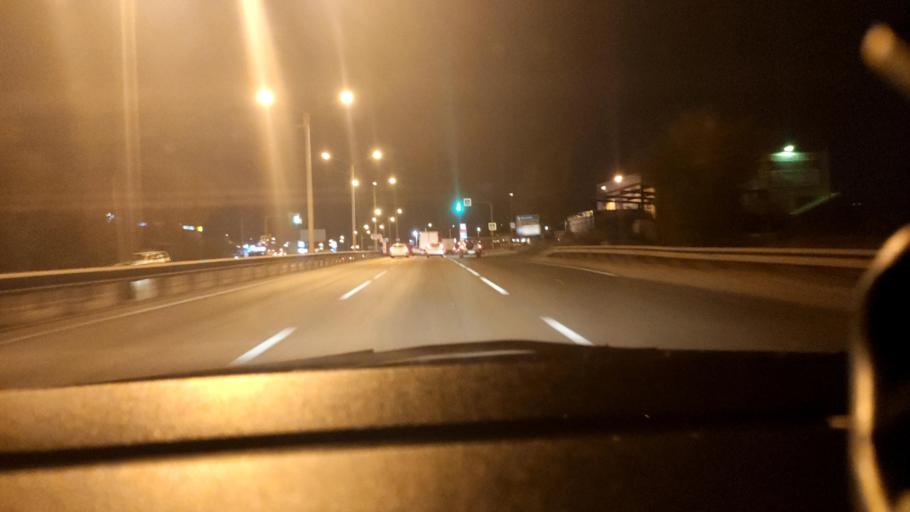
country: RU
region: Voronezj
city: Voronezh
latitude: 51.6657
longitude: 39.1277
